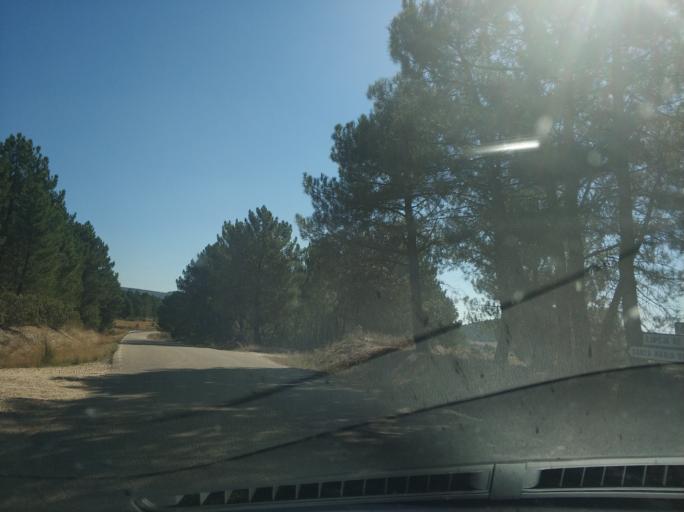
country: ES
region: Castille and Leon
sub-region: Provincia de Soria
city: Santa Maria de las Hoyas
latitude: 41.7762
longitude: -3.1814
